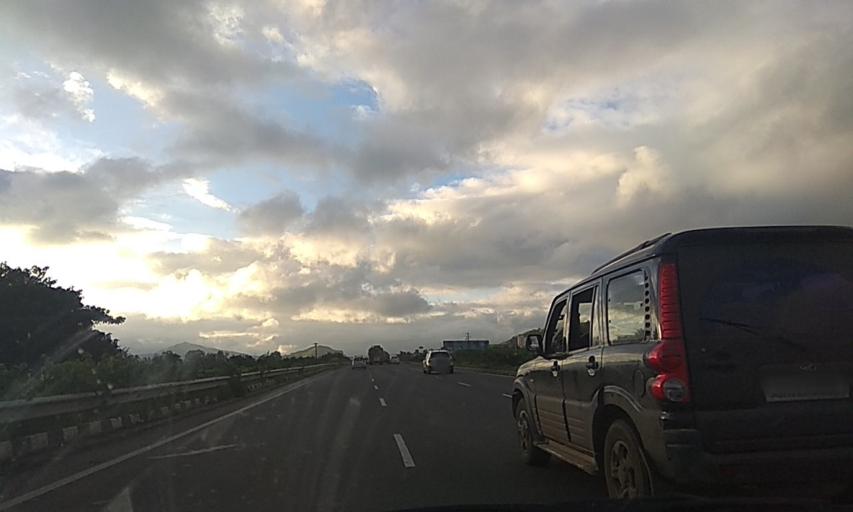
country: IN
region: Maharashtra
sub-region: Satara Division
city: Satara
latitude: 17.7335
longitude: 74.0141
